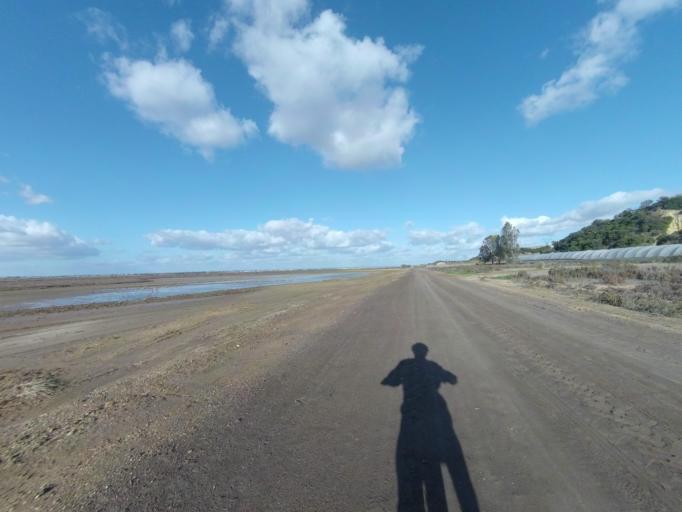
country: ES
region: Andalusia
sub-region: Provincia de Huelva
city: Palos de la Frontera
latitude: 37.2599
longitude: -6.8725
